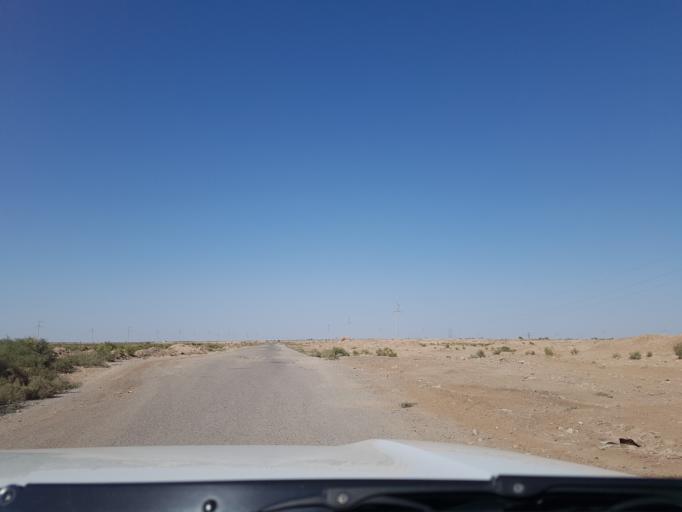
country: IR
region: Razavi Khorasan
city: Sarakhs
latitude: 36.5256
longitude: 61.2420
